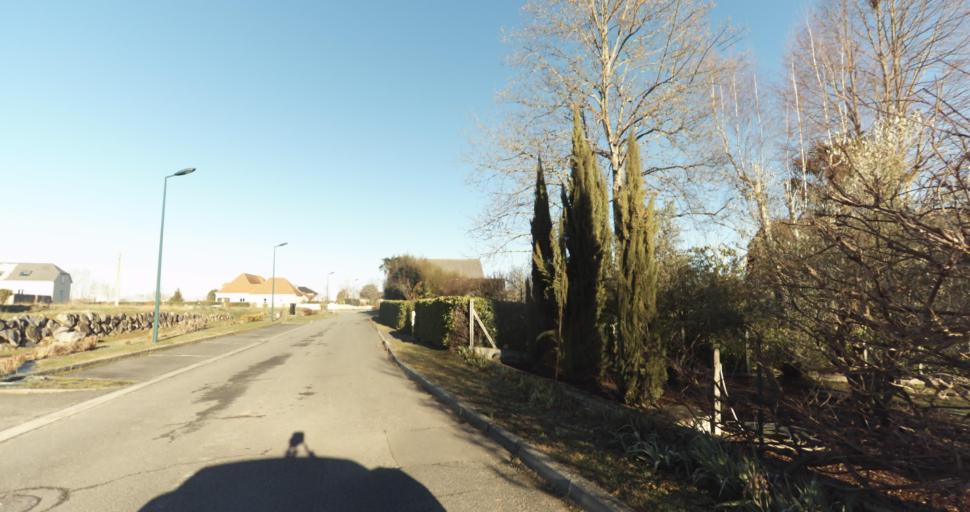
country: FR
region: Aquitaine
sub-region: Departement des Pyrenees-Atlantiques
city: Morlaas
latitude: 43.3282
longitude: -0.2596
